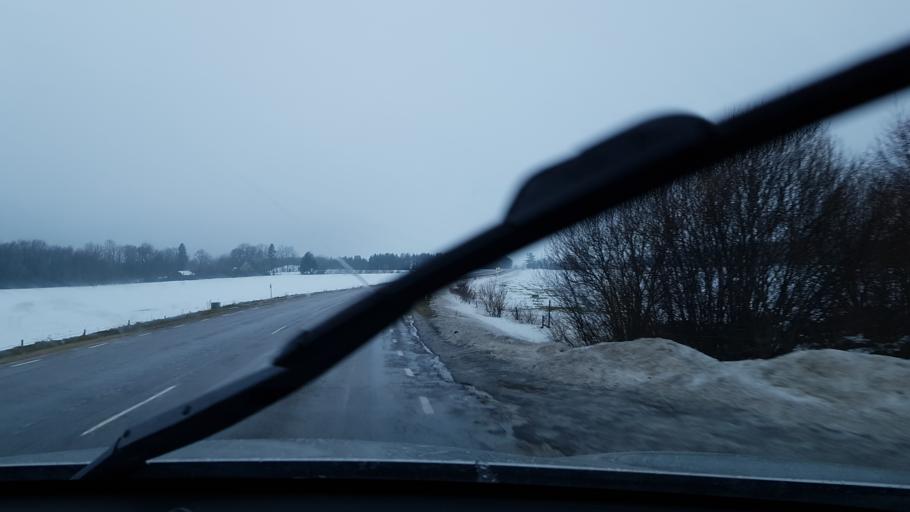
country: EE
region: Harju
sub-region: Nissi vald
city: Turba
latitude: 58.9096
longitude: 24.1422
